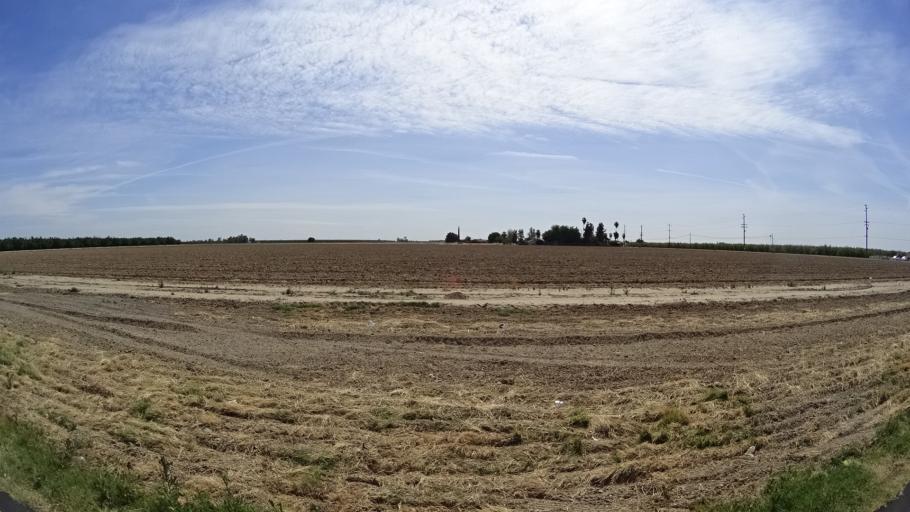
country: US
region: California
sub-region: Kings County
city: Hanford
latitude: 36.3437
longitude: -119.6234
